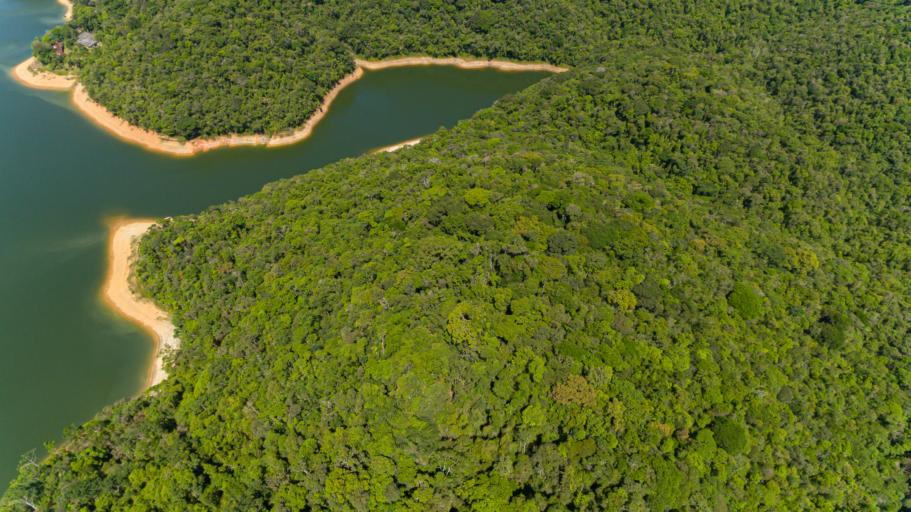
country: BR
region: Sao Paulo
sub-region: Juquitiba
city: Juquitiba
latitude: -24.0252
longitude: -47.2482
